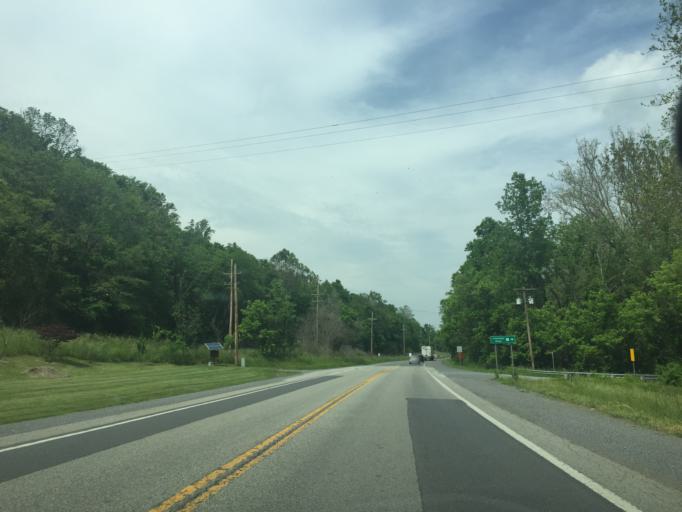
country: US
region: West Virginia
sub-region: Morgan County
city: Berkeley Springs
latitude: 39.6401
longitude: -78.2197
